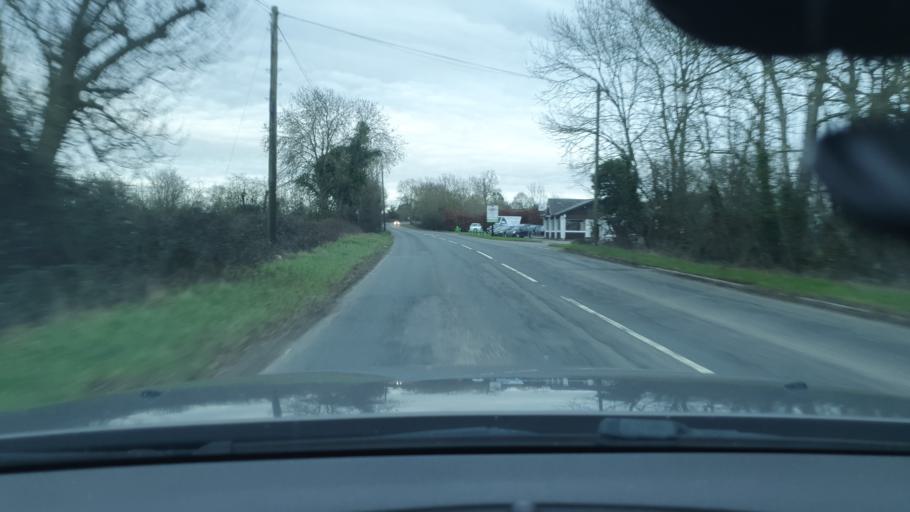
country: GB
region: England
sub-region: Wiltshire
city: Melksham
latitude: 51.3385
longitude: -2.1278
